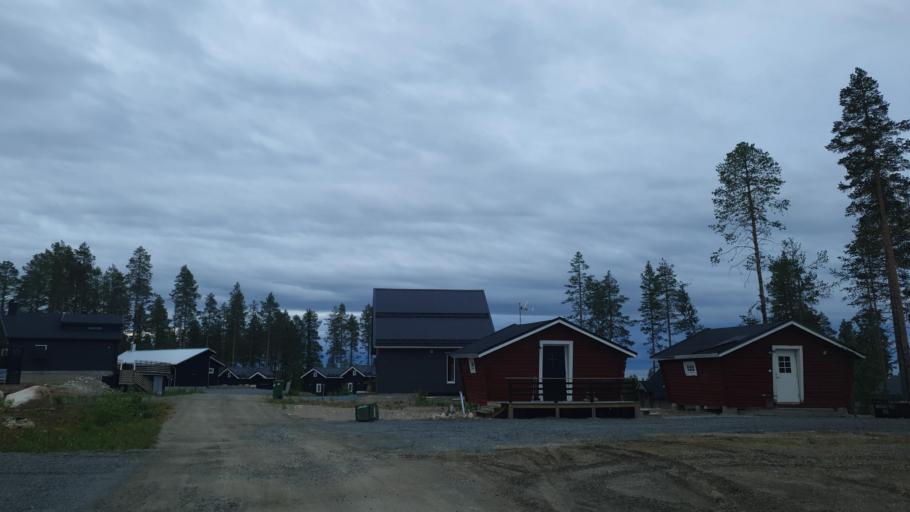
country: SE
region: Norrbotten
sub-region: Jokkmokks Kommun
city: Jokkmokk
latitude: 66.1526
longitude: 19.9928
